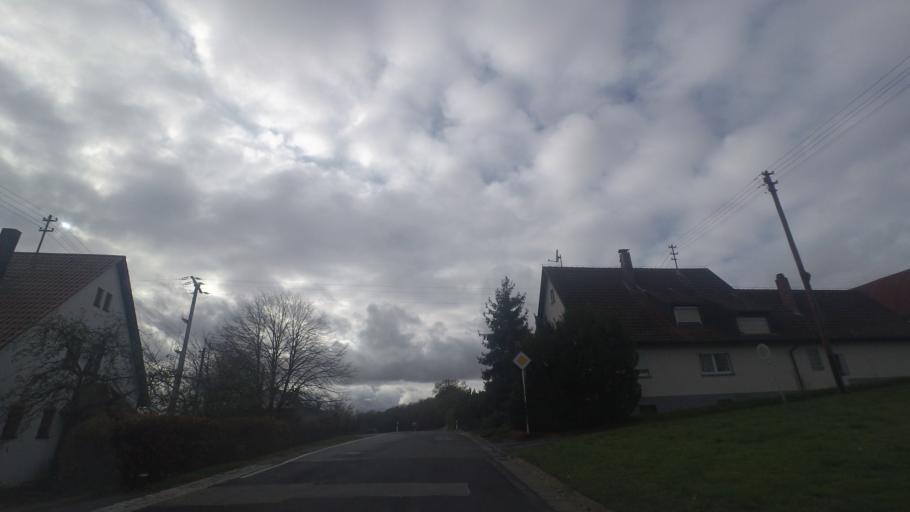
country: DE
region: Bavaria
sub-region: Regierungsbezirk Unterfranken
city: Hochheim
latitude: 50.3637
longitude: 10.4456
